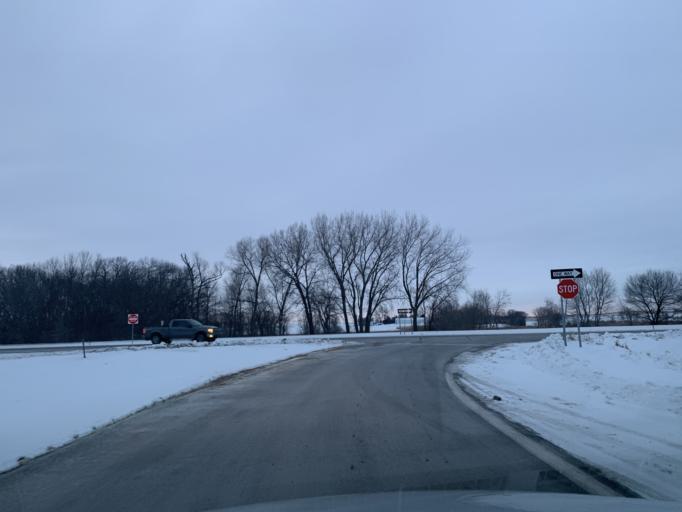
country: US
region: Minnesota
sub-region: Carver County
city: Cologne
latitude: 44.7751
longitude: -93.7551
